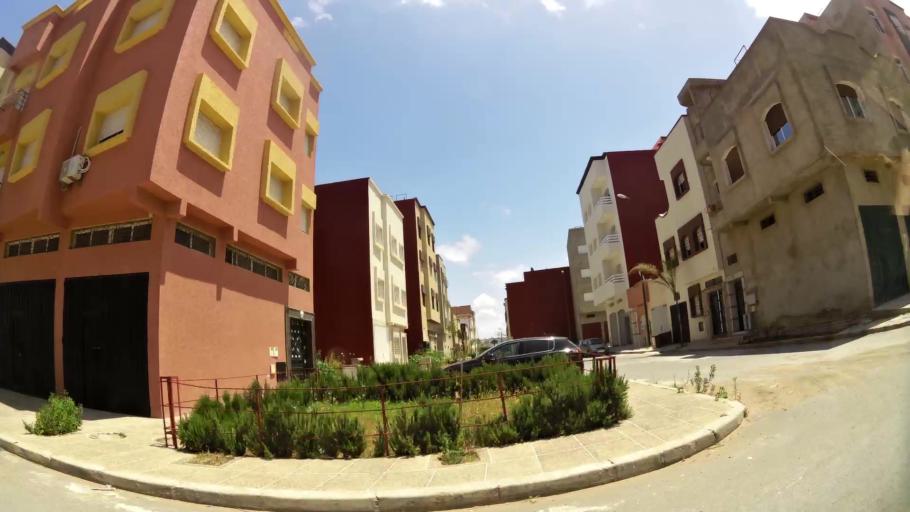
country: MA
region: Gharb-Chrarda-Beni Hssen
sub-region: Kenitra Province
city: Kenitra
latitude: 34.2723
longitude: -6.6186
